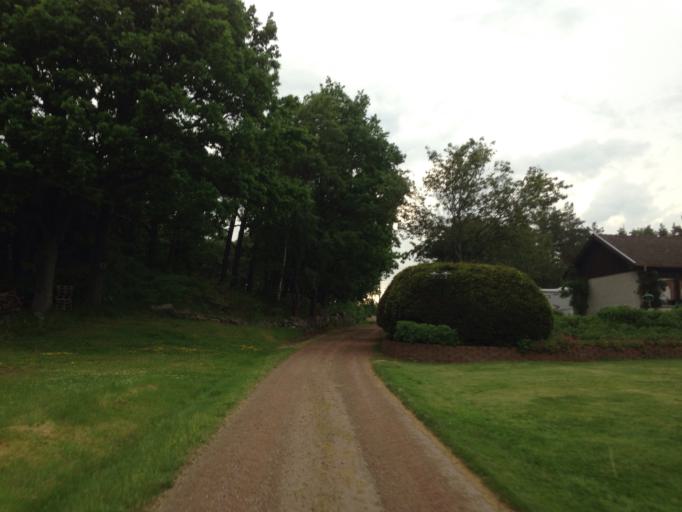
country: SE
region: Vaestra Goetaland
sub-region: Kungalvs Kommun
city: Kungalv
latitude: 57.8052
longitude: 11.8886
